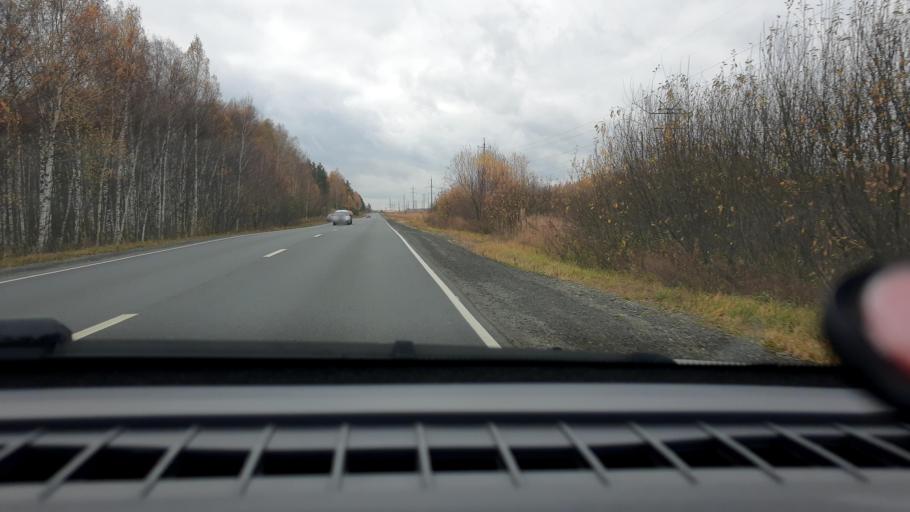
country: RU
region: Nizjnij Novgorod
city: Lukino
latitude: 56.3533
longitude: 43.5898
